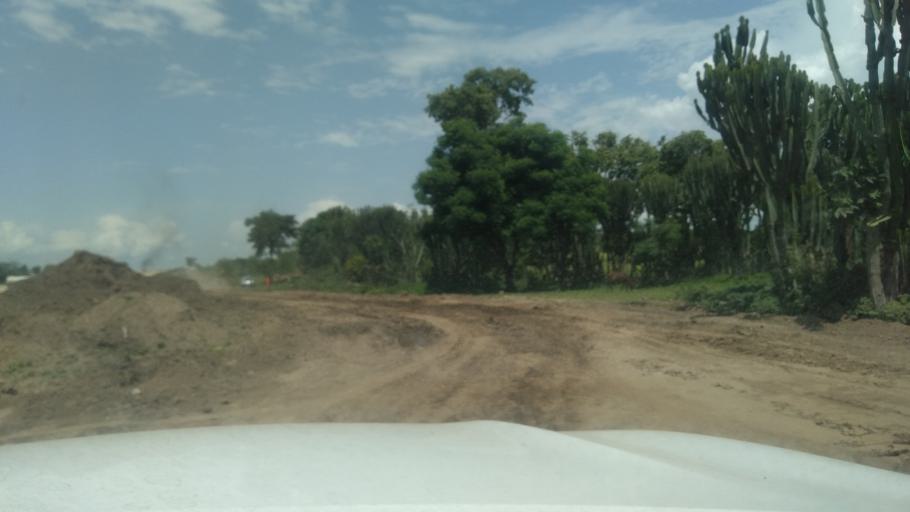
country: ET
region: Oromiya
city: Shashemene
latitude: 7.2804
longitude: 38.6052
